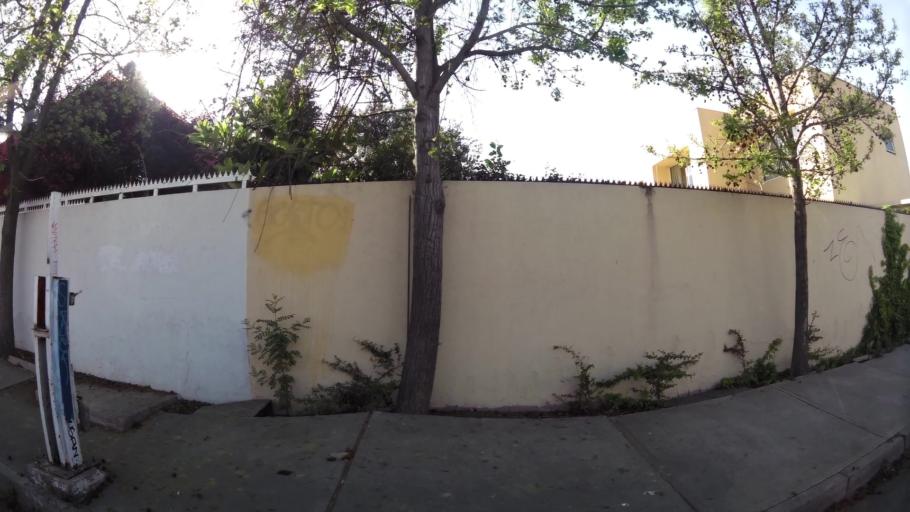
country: CL
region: Santiago Metropolitan
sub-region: Provincia de Santiago
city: Villa Presidente Frei, Nunoa, Santiago, Chile
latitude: -33.4838
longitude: -70.5551
